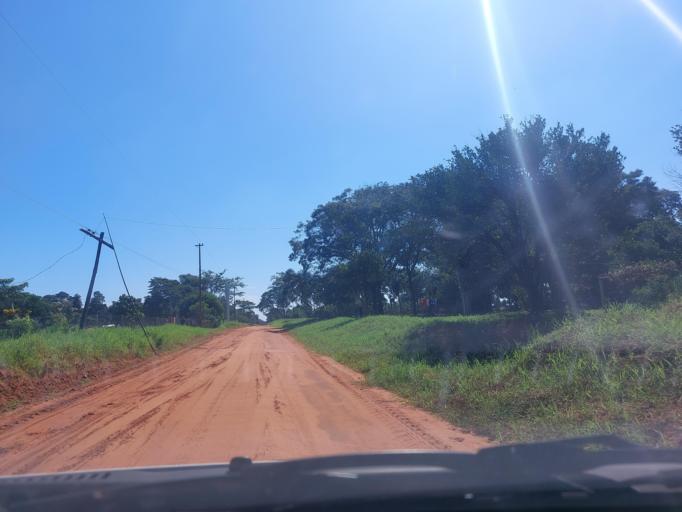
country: PY
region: San Pedro
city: Lima
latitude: -24.1548
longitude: -56.0114
